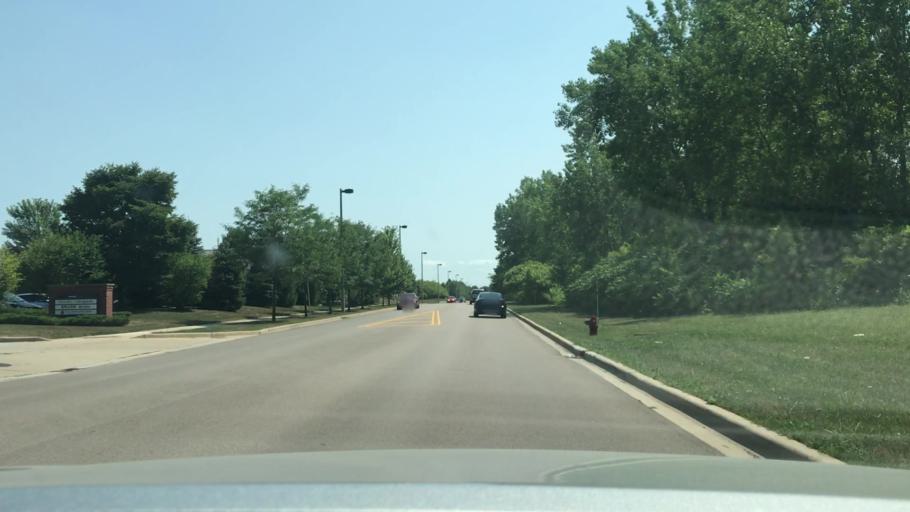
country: US
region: Illinois
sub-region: Kane County
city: Aurora
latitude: 41.7411
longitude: -88.2302
